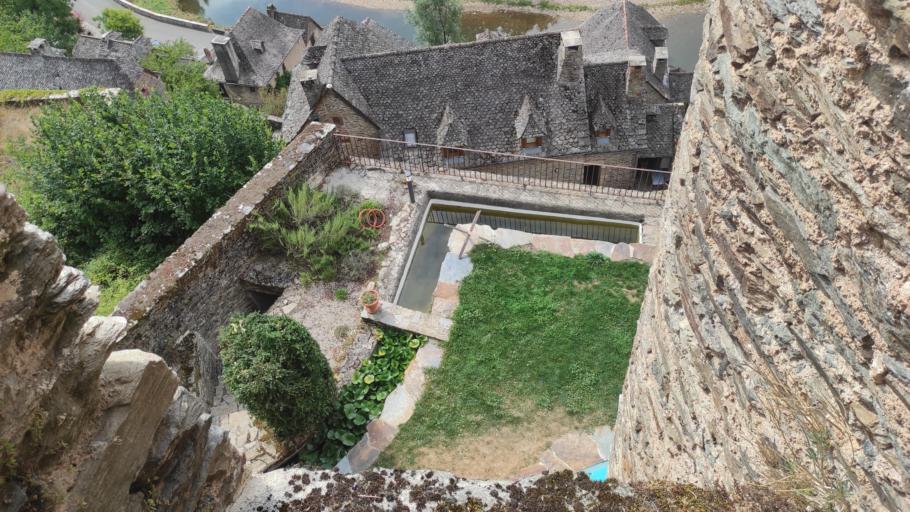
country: FR
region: Midi-Pyrenees
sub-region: Departement de l'Aveyron
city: Colombies
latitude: 44.3888
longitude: 2.3360
